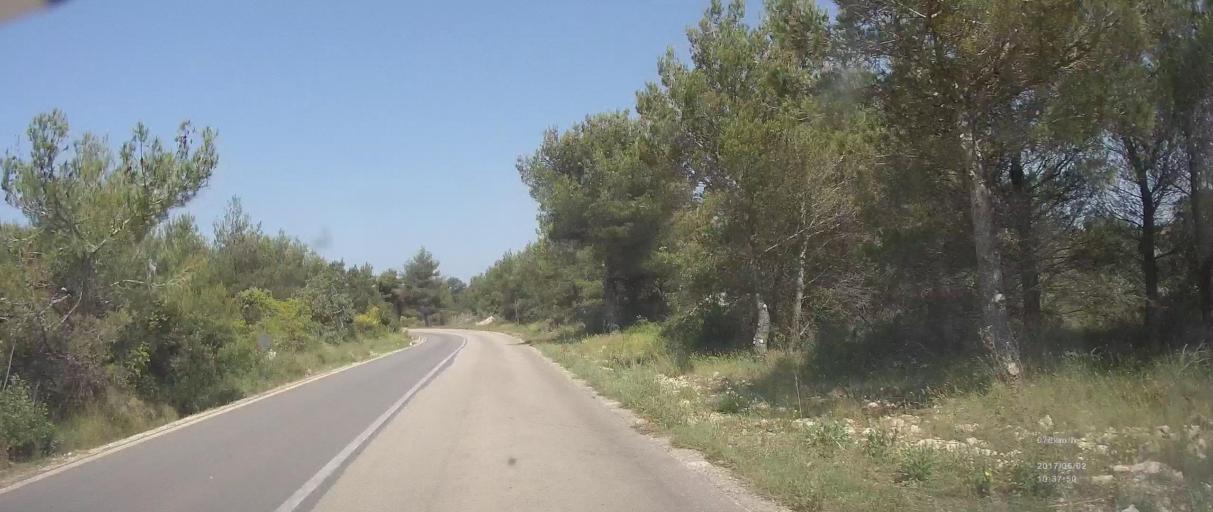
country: HR
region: Sibensko-Kniniska
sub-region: Grad Sibenik
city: Sibenik
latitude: 43.7023
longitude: 15.8936
